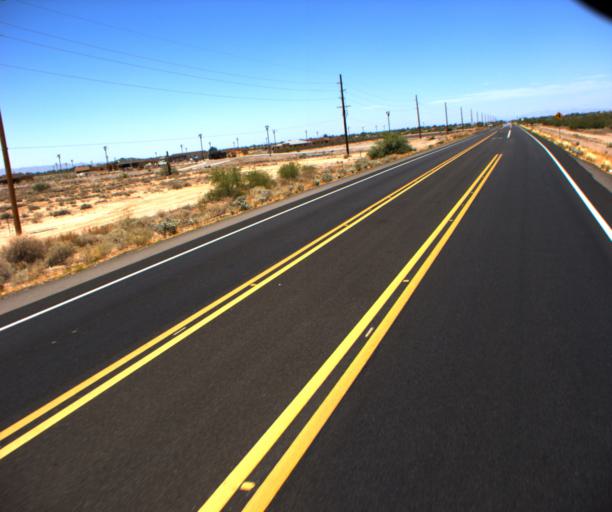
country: US
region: Arizona
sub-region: Maricopa County
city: Sun Lakes
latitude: 33.1826
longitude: -111.8409
